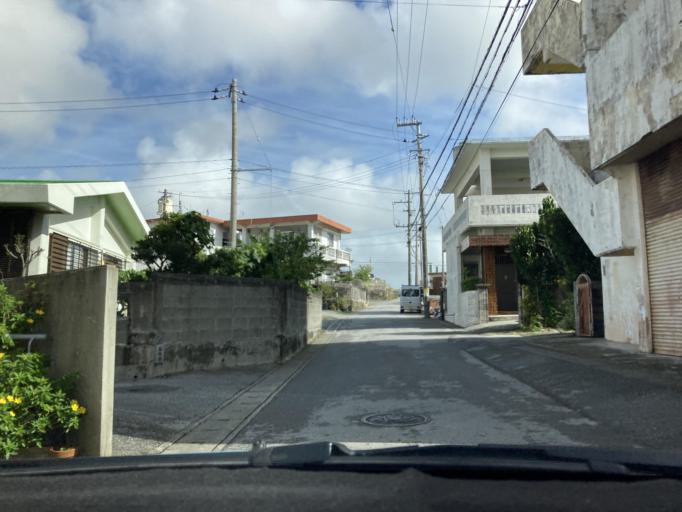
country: JP
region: Okinawa
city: Naha-shi
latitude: 26.2029
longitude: 127.7302
